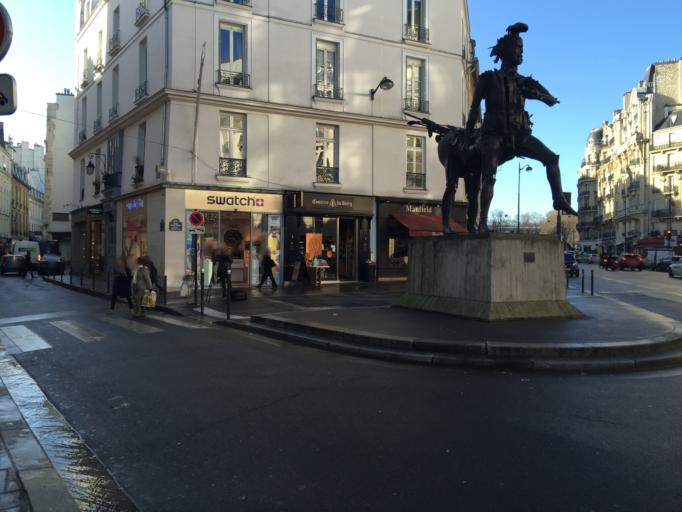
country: FR
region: Ile-de-France
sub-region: Paris
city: Paris
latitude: 48.8521
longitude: 2.3298
